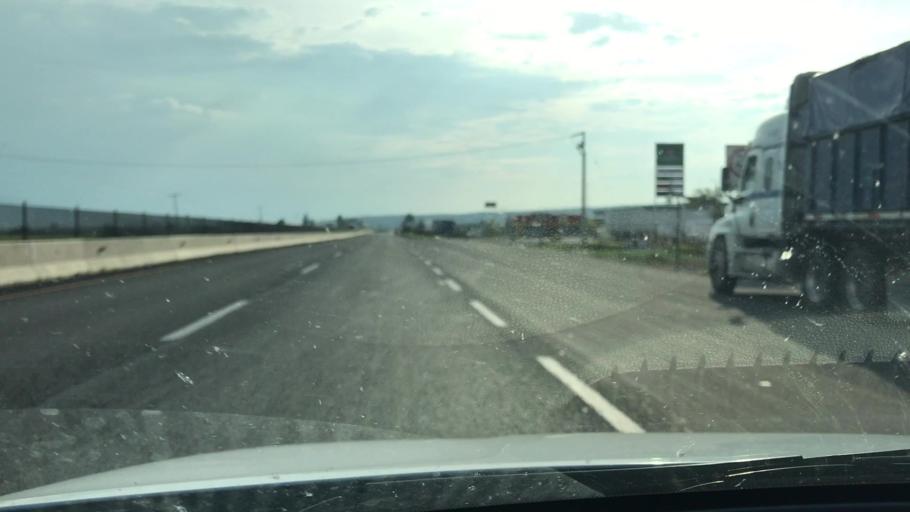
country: MX
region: Guanajuato
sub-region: Penjamo
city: Estacion la Piedad
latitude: 20.3888
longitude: -101.9337
